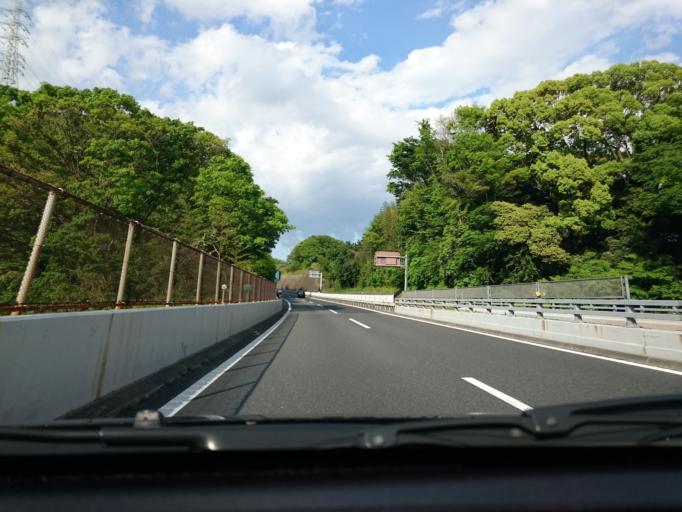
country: JP
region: Kanagawa
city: Ninomiya
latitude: 35.3215
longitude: 139.2775
